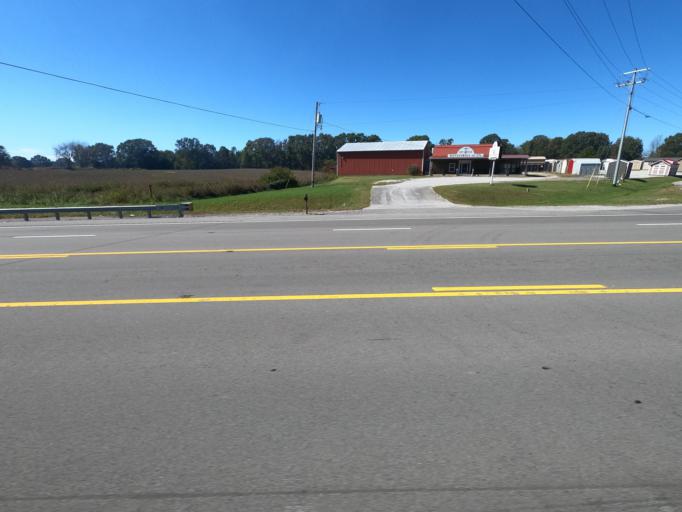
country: US
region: Tennessee
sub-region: Maury County
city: Mount Pleasant
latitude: 35.4267
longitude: -87.2816
